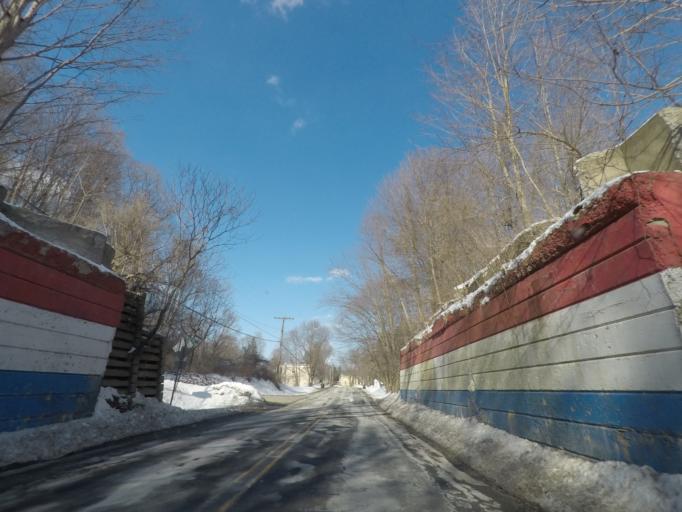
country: US
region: New York
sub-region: Saratoga County
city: Stillwater
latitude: 42.8963
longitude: -73.5646
